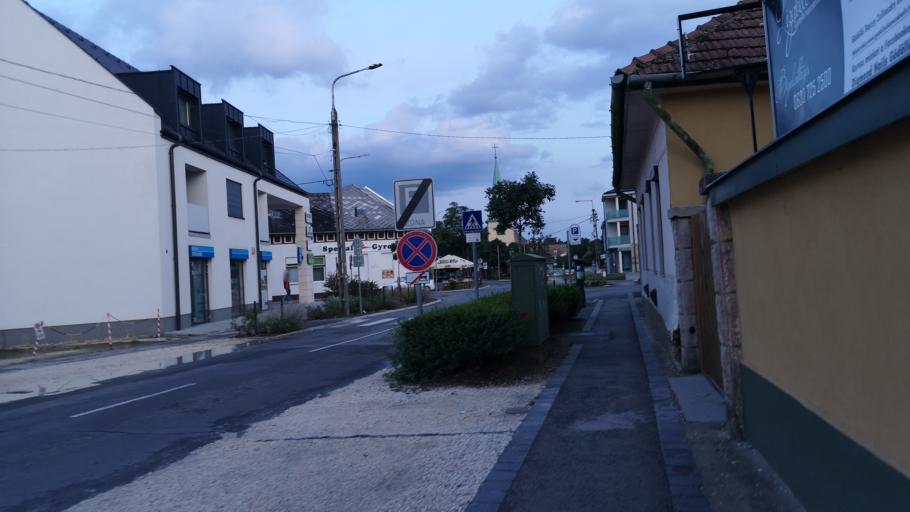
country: HU
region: Pest
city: Godollo
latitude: 47.6022
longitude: 19.3474
